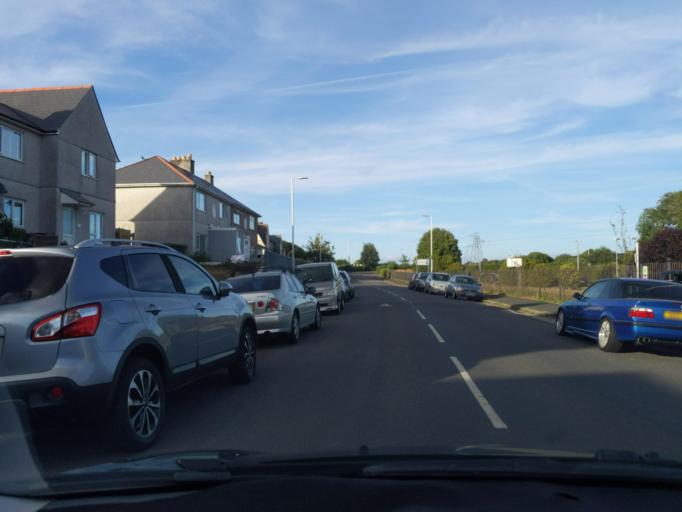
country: GB
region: England
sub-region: Plymouth
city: Plymstock
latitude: 50.3755
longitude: -4.1121
